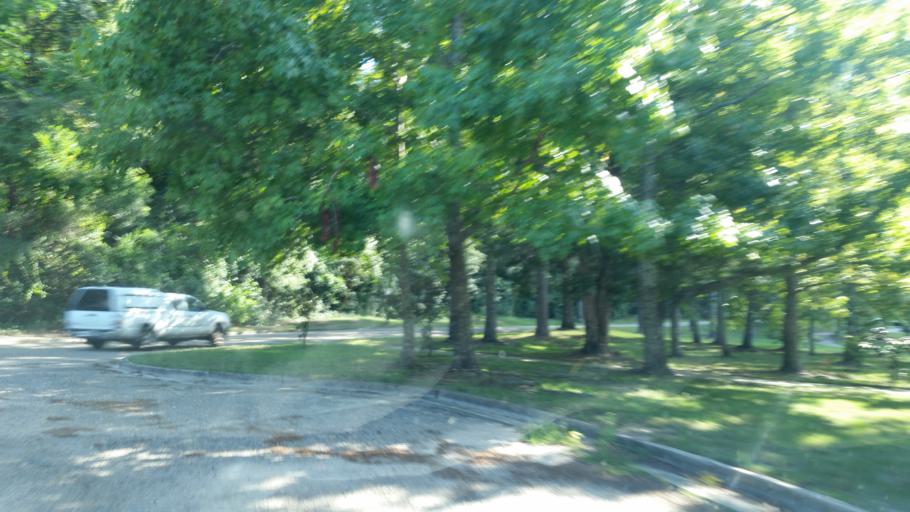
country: US
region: Alabama
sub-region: Mobile County
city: Prichard
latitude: 30.7051
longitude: -88.1519
